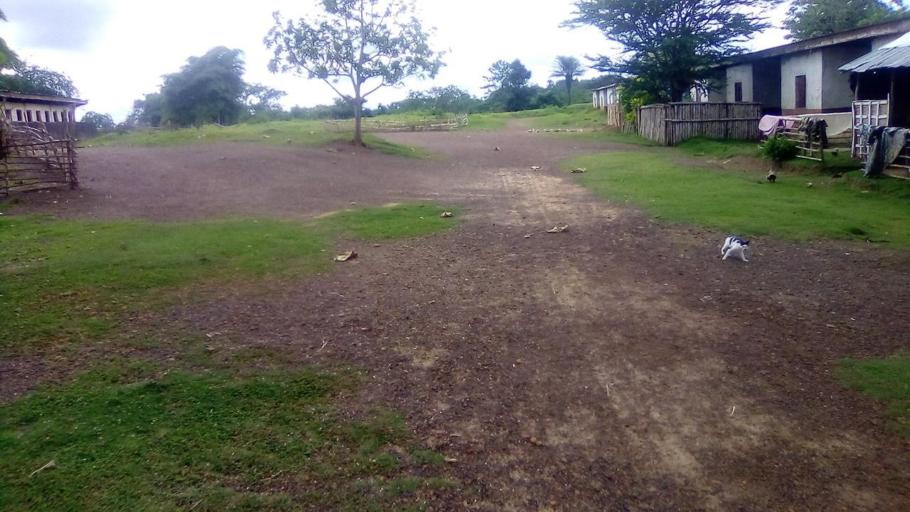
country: SL
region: Southern Province
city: Pujehun
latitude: 7.3727
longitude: -11.7254
